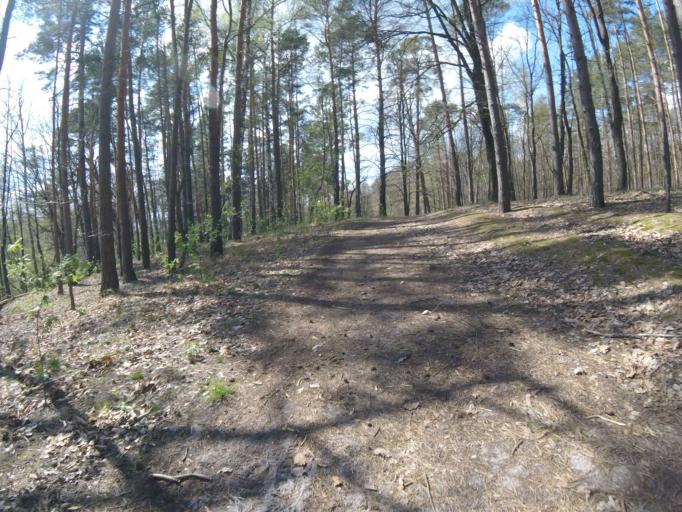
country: DE
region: Brandenburg
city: Gross Koris
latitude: 52.2014
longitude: 13.7147
